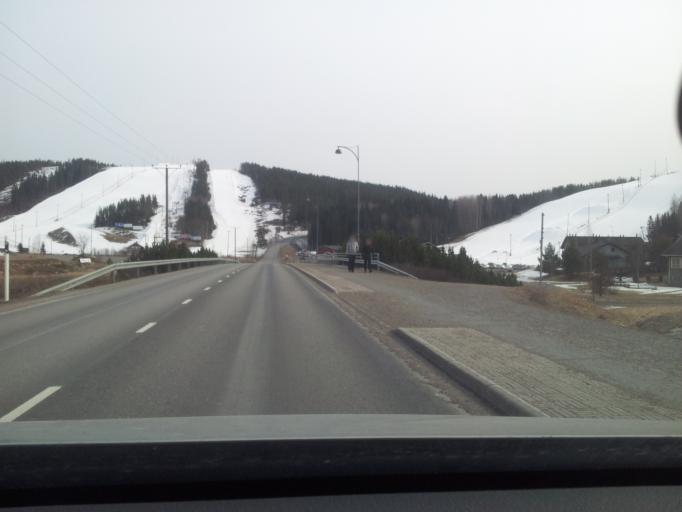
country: FI
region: Central Finland
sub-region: Jaemsae
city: Jaemsae
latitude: 61.8815
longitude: 25.2961
